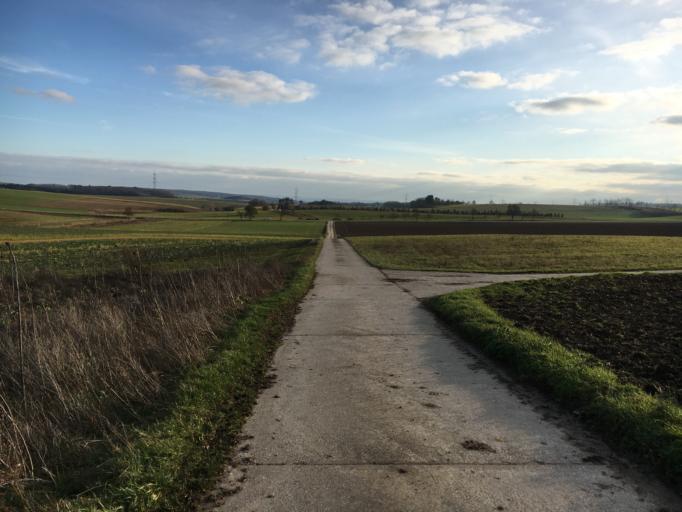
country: DE
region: Baden-Wuerttemberg
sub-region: Karlsruhe Region
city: Mosbach
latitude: 49.3763
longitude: 9.2025
